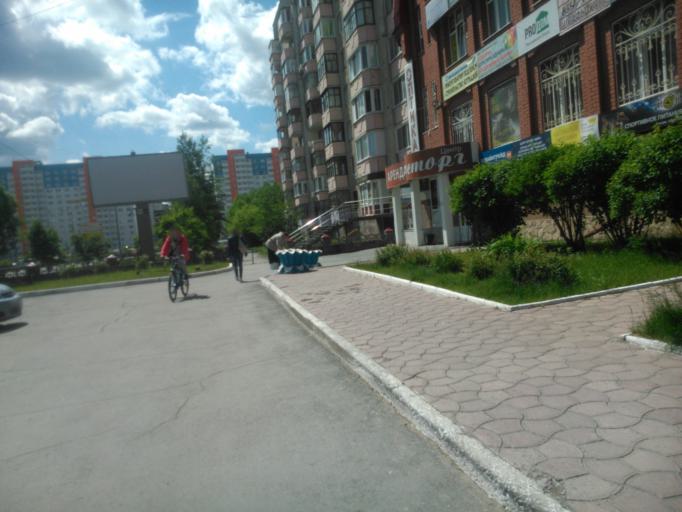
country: RU
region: Tjumen
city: Tyumen
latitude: 57.1049
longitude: 65.6032
